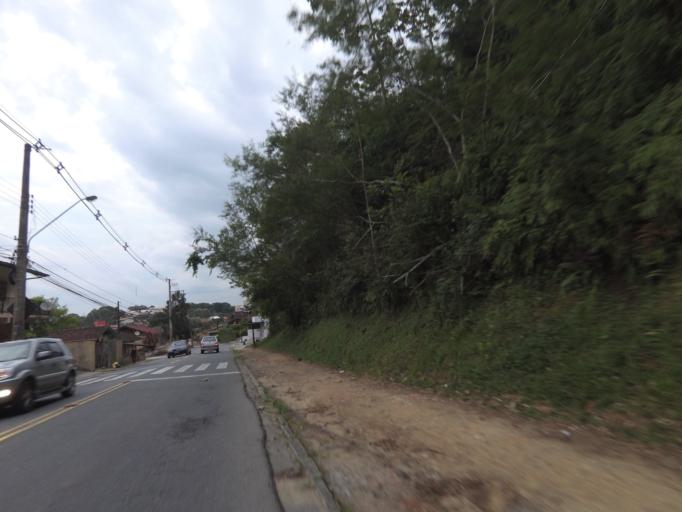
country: BR
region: Santa Catarina
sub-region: Blumenau
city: Blumenau
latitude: -26.8777
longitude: -49.0588
